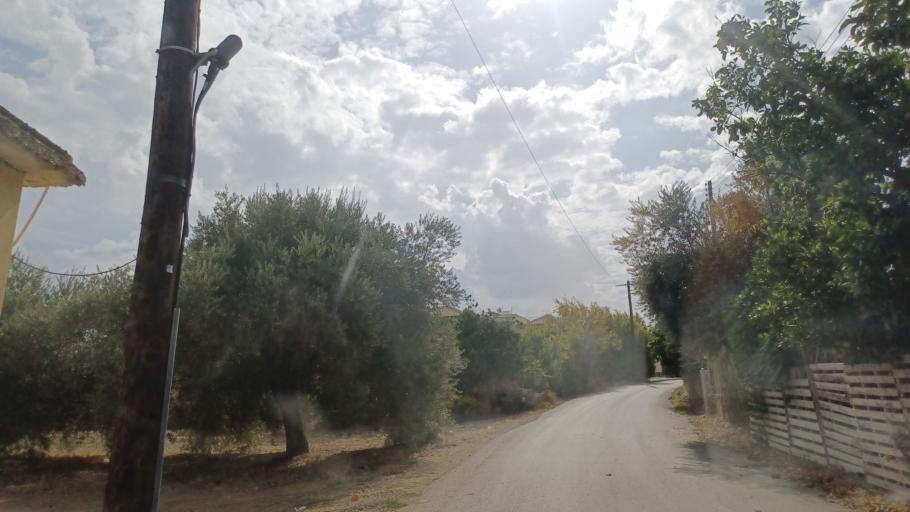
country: CY
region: Pafos
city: Polis
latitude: 35.0264
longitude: 32.4197
